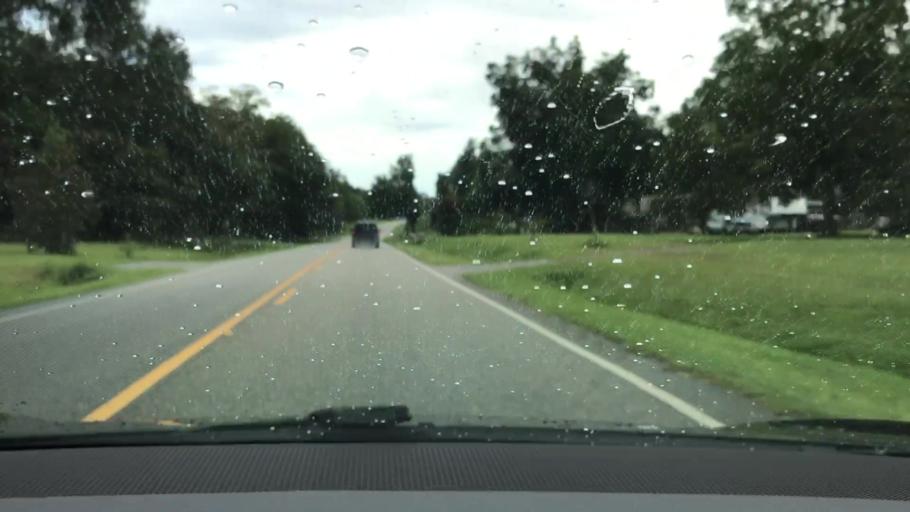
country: US
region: Alabama
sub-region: Geneva County
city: Samson
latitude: 31.0853
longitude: -86.1075
